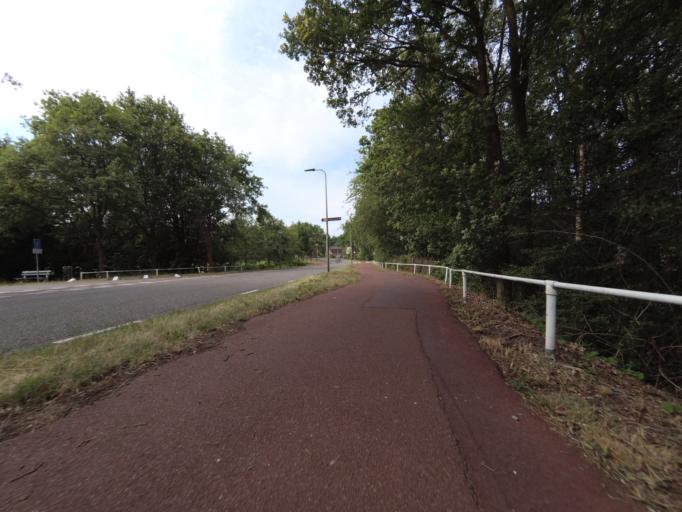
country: NL
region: Overijssel
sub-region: Gemeente Hengelo
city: Hengelo
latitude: 52.2130
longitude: 6.8029
